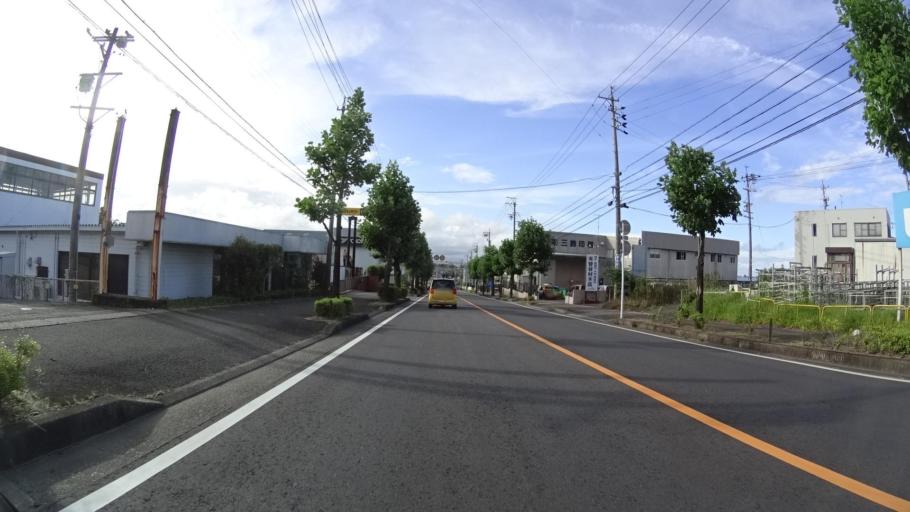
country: JP
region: Mie
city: Kawage
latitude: 34.8540
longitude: 136.5336
